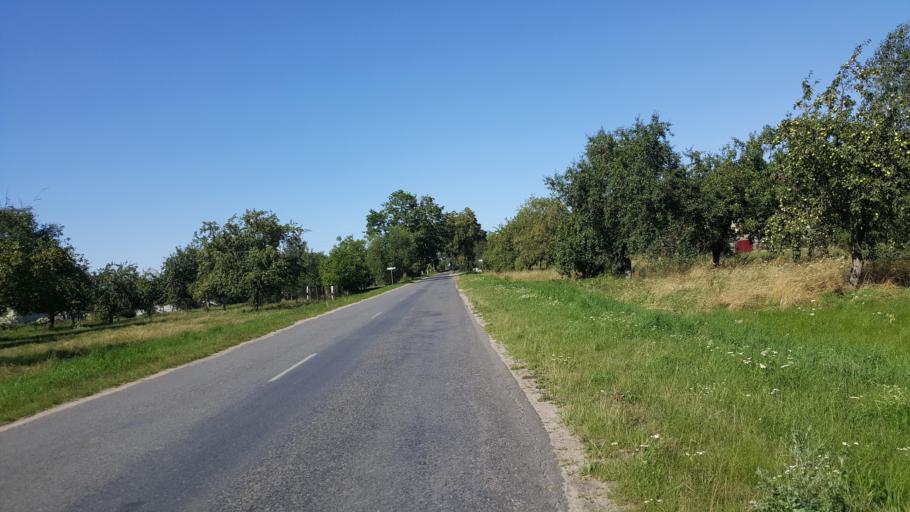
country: BY
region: Brest
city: Charnawchytsy
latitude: 52.2089
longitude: 23.7370
